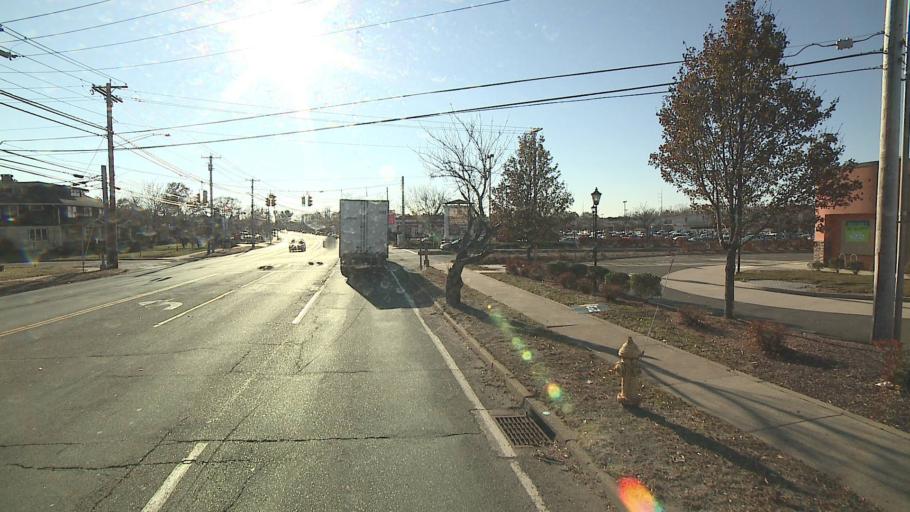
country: US
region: Connecticut
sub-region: New Haven County
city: North Haven
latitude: 41.3940
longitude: -72.8576
